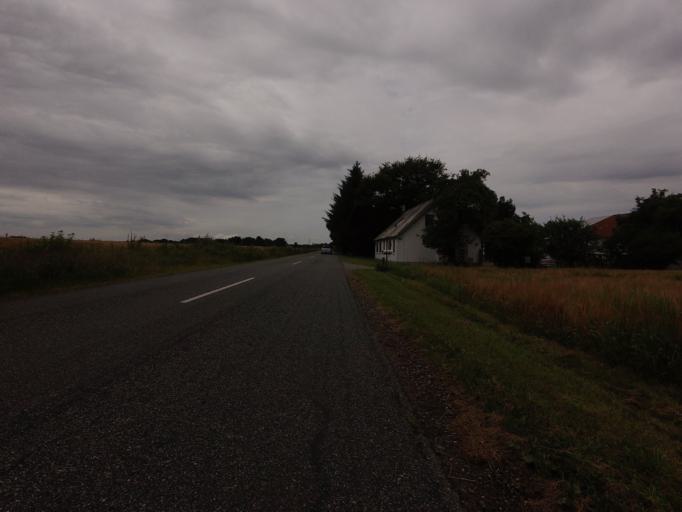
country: DK
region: North Denmark
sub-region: Alborg Kommune
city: Vadum
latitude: 57.1311
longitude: 9.8486
